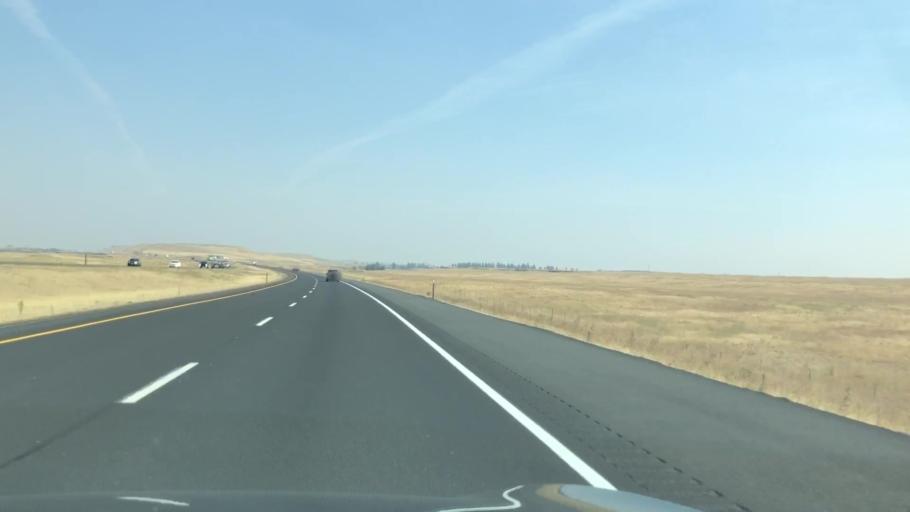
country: US
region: Washington
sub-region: Spokane County
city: Medical Lake
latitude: 47.3335
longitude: -117.9141
